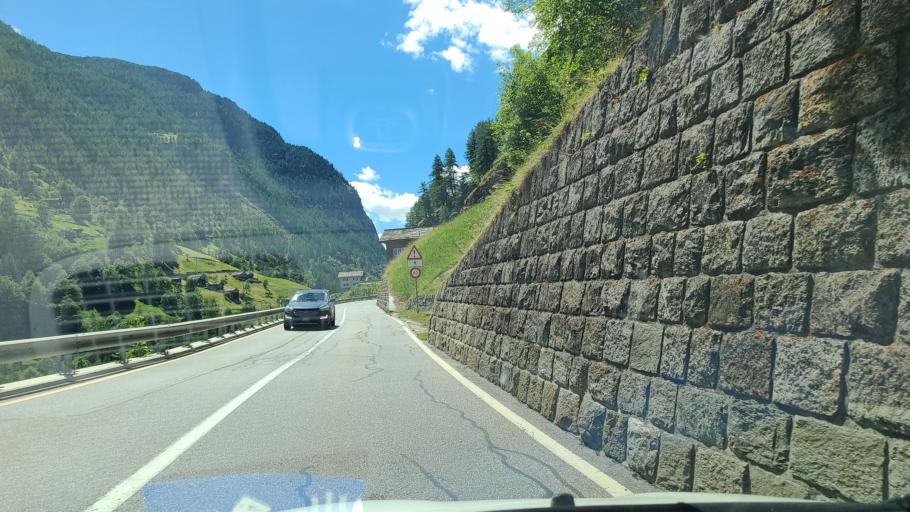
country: CH
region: Valais
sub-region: Visp District
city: Stalden
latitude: 46.1933
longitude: 7.8979
